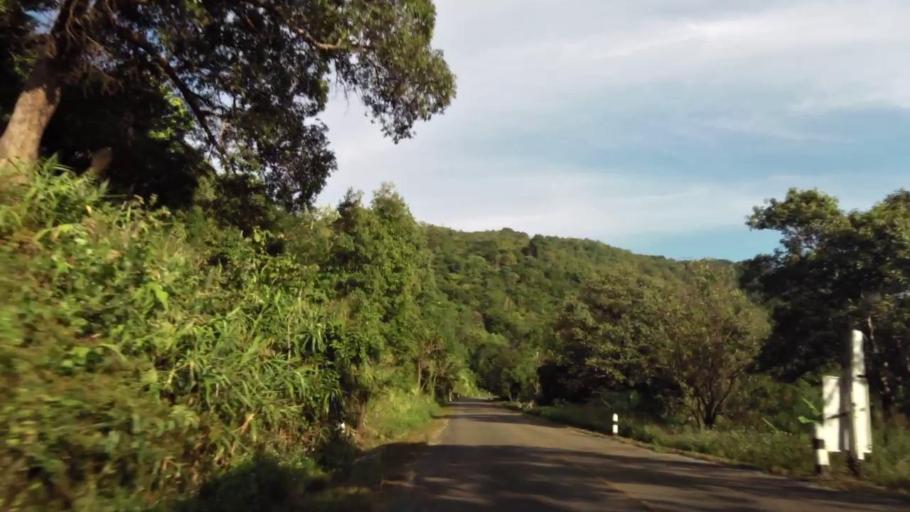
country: TH
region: Chiang Rai
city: Khun Tan
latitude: 19.8558
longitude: 100.4346
